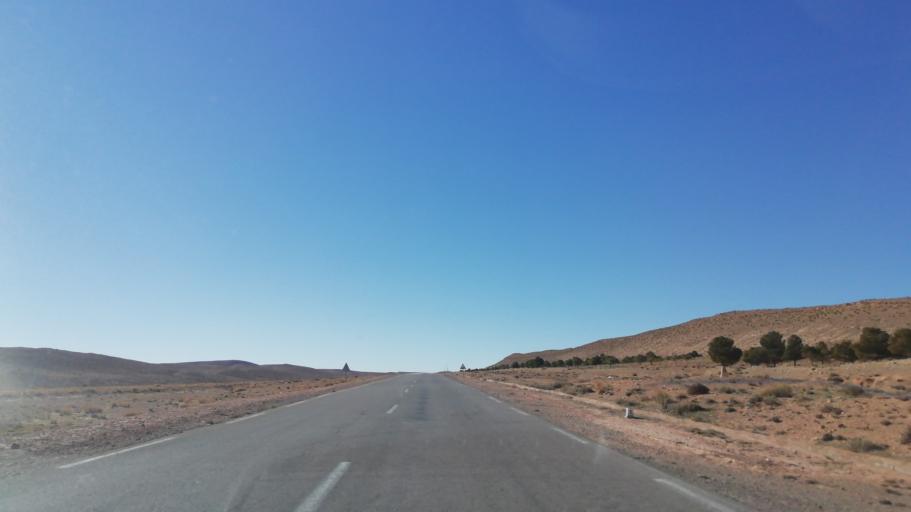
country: DZ
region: El Bayadh
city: El Bayadh
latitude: 33.6865
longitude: 1.4602
